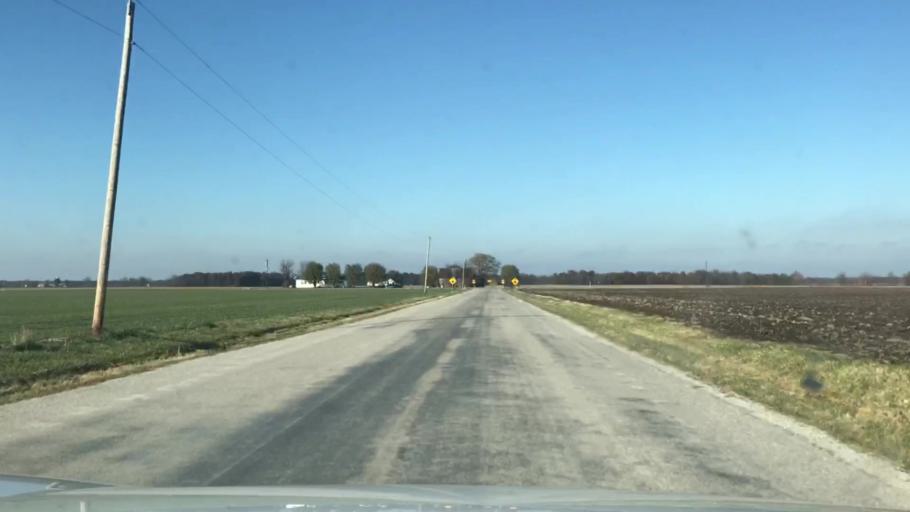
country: US
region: Illinois
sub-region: Washington County
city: Okawville
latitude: 38.4390
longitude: -89.4780
